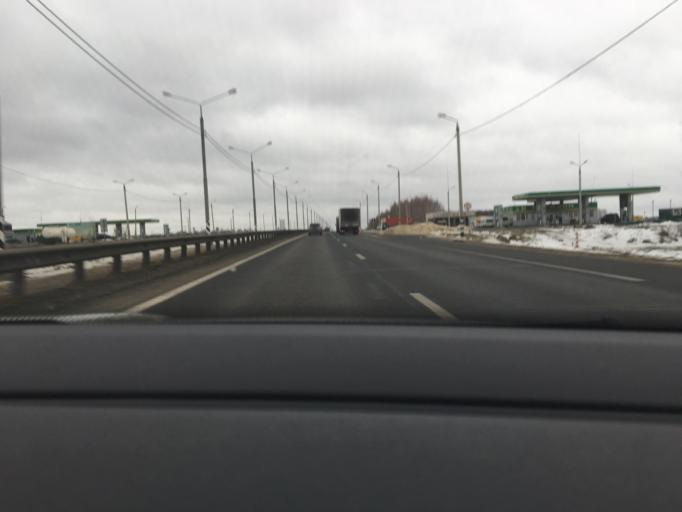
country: RU
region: Tula
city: Zaokskiy
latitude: 54.8061
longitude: 37.4837
